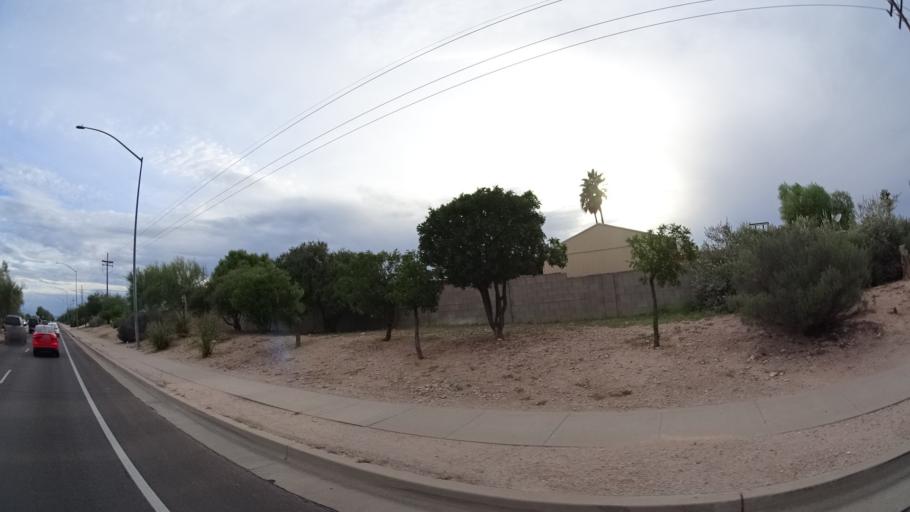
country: US
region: Arizona
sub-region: Pima County
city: South Tucson
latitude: 32.1612
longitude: -110.9350
